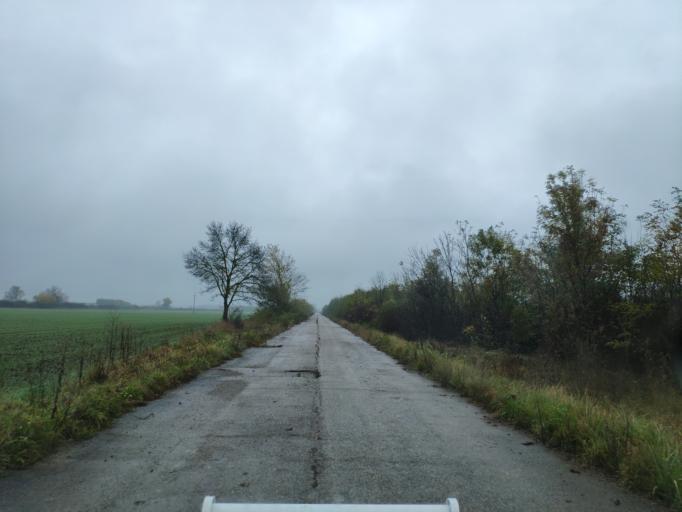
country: SK
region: Kosicky
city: Cierna nad Tisou
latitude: 48.4293
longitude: 22.0028
